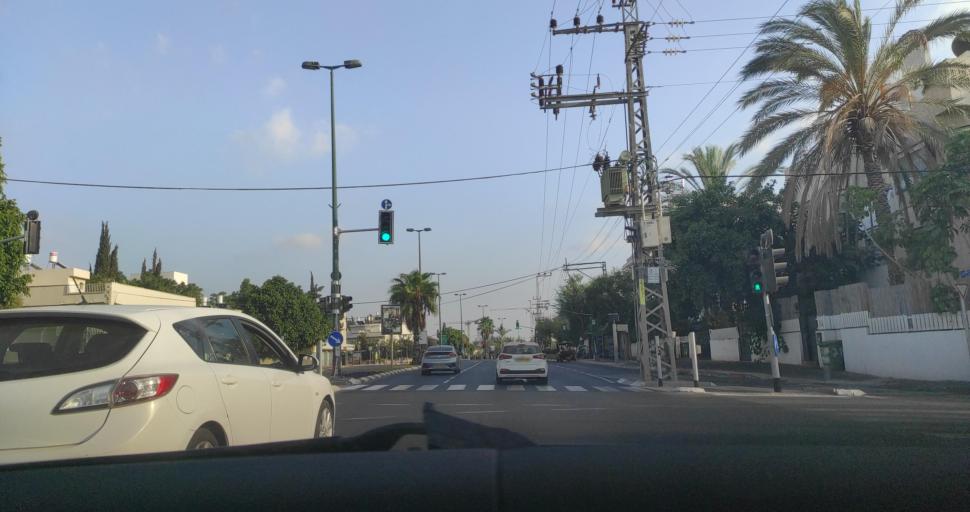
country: IL
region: Tel Aviv
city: Bene Beraq
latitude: 32.1105
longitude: 34.8256
